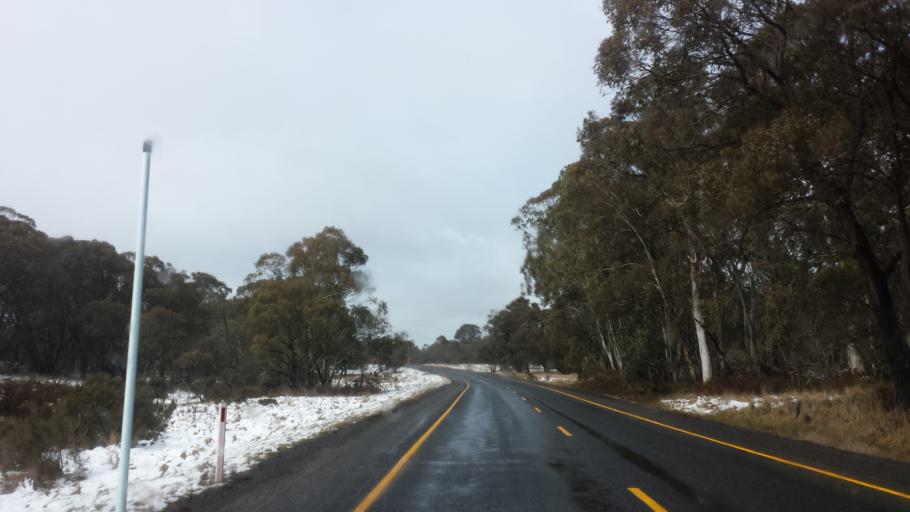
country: AU
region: Victoria
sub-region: Alpine
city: Mount Beauty
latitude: -37.0408
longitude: 147.3091
